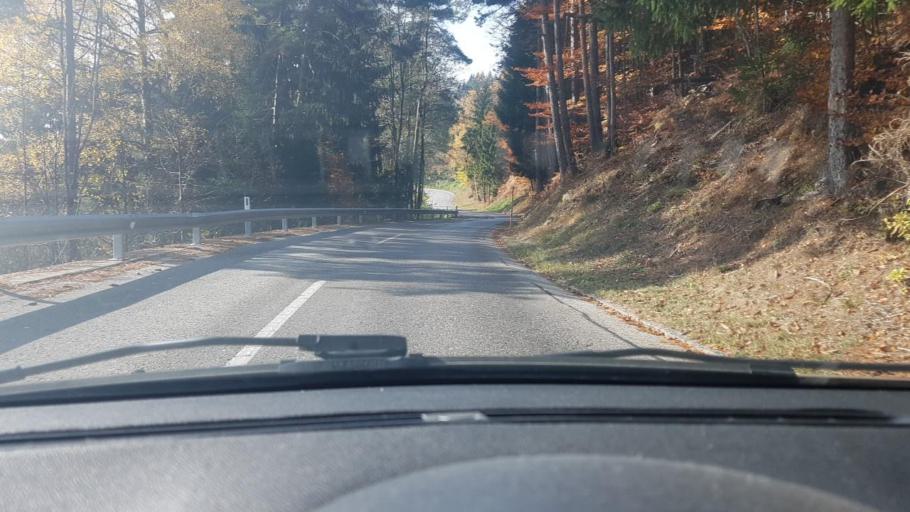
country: AT
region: Carinthia
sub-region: Politischer Bezirk Klagenfurt Land
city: Maria Worth
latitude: 46.6039
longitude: 14.1430
